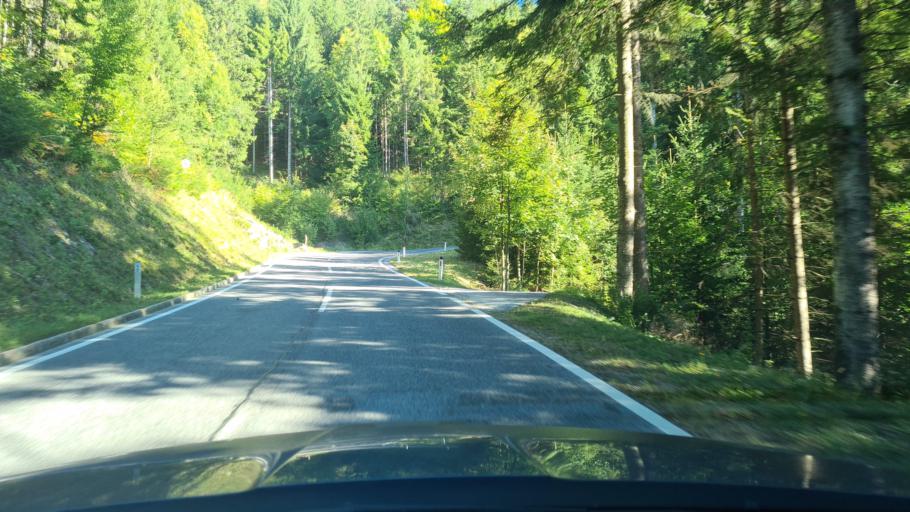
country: AT
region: Styria
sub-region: Politischer Bezirk Weiz
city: Passail
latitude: 47.2989
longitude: 15.4812
